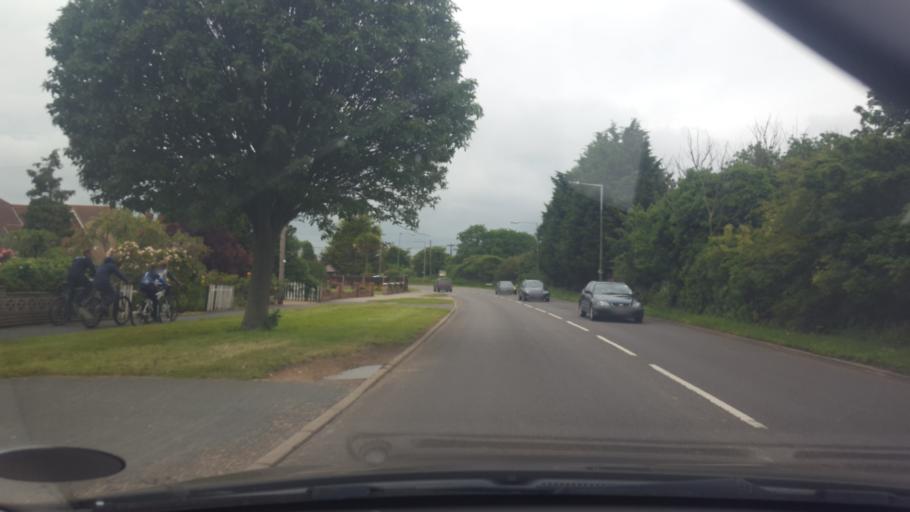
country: GB
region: England
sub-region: Essex
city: Clacton-on-Sea
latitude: 51.7876
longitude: 1.1197
